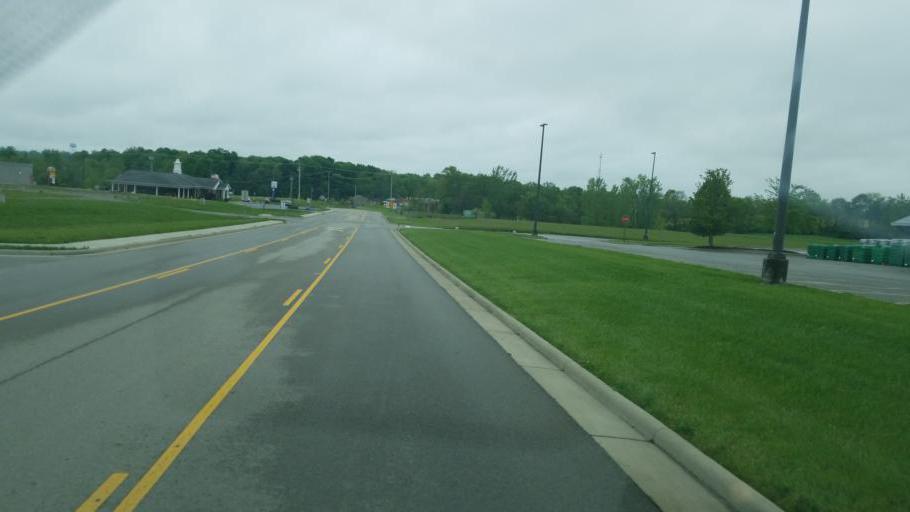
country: US
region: Ohio
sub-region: Highland County
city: Hillsboro
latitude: 39.2273
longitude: -83.6252
